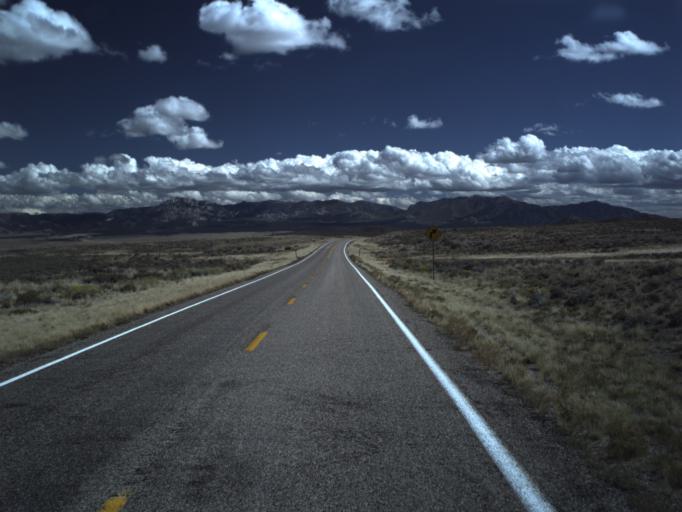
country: US
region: Utah
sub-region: Beaver County
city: Milford
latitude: 38.4346
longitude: -113.1369
